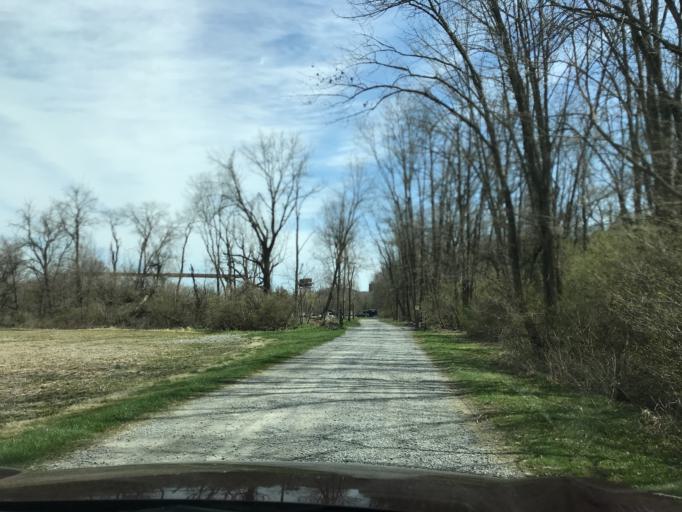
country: US
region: Pennsylvania
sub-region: Northumberland County
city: Northumberland
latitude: 40.9045
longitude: -76.8463
